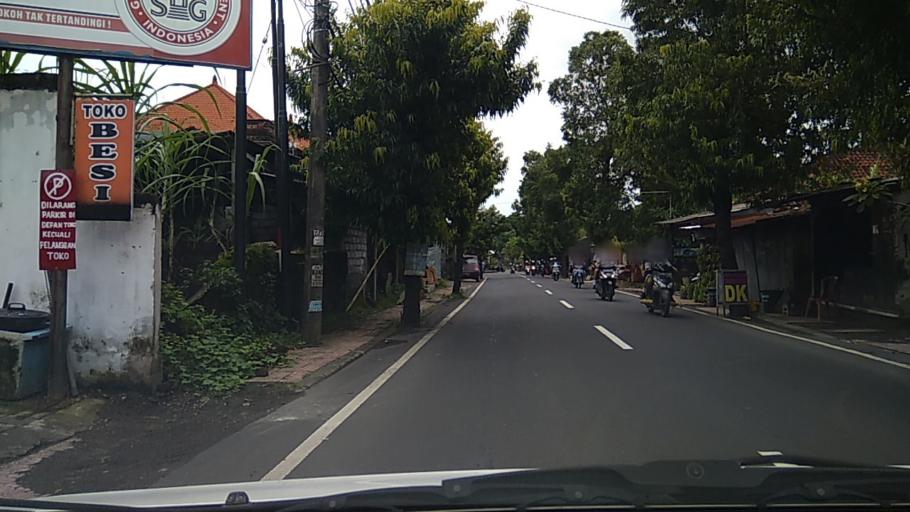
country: ID
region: Bali
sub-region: Kabupaten Gianyar
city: Ubud
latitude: -8.5249
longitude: 115.2920
